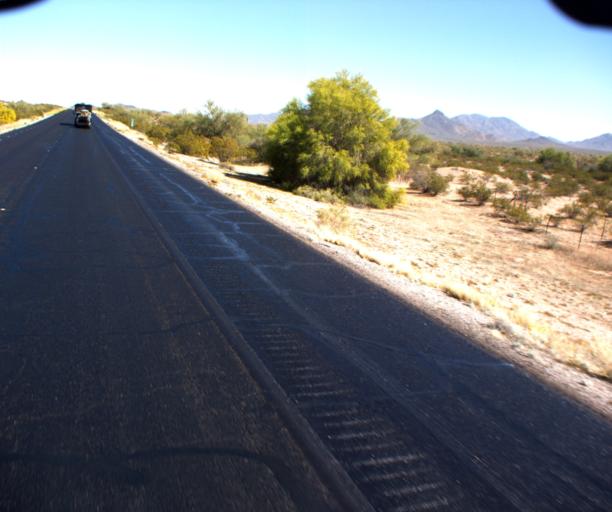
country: US
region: Arizona
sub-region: Pinal County
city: Maricopa
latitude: 32.8392
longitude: -112.2320
